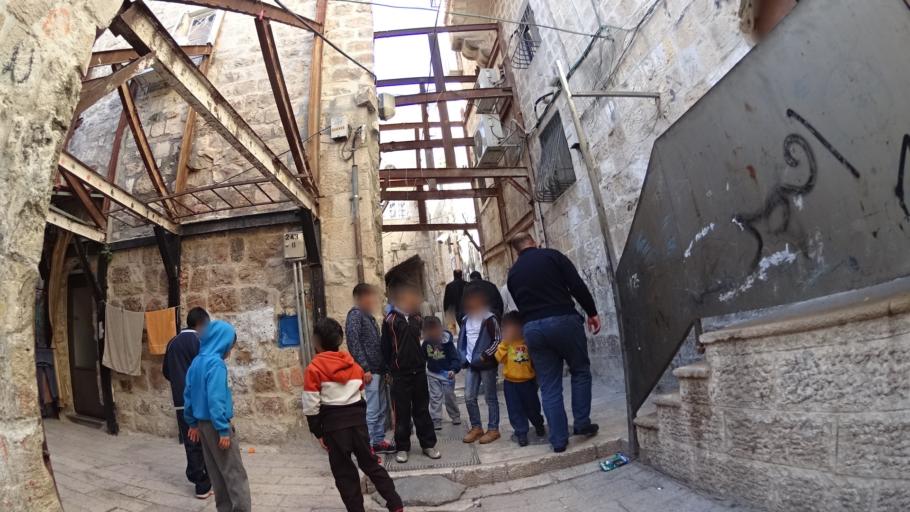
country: PS
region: West Bank
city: Old City
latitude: 31.7782
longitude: 35.2318
